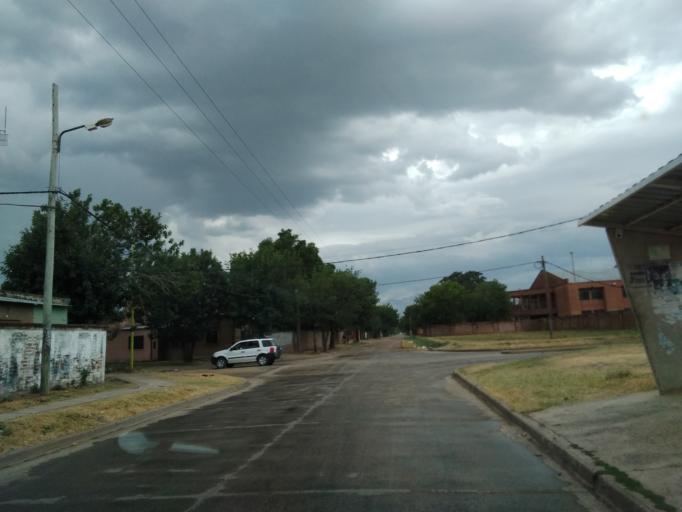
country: AR
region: Corrientes
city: Corrientes
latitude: -27.5227
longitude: -58.7887
